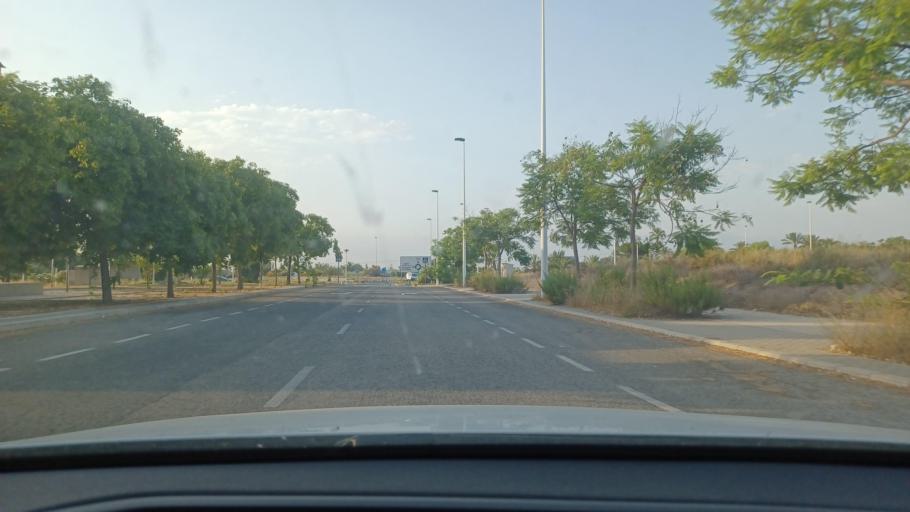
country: ES
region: Valencia
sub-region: Provincia de Alicante
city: Elche
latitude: 38.2857
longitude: -0.6241
